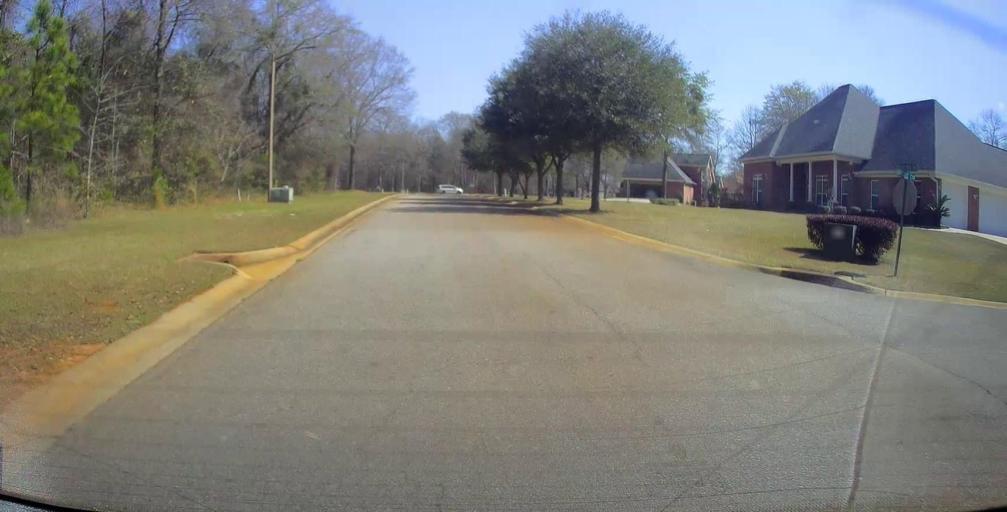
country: US
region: Georgia
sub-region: Peach County
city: Byron
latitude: 32.5976
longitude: -83.7527
